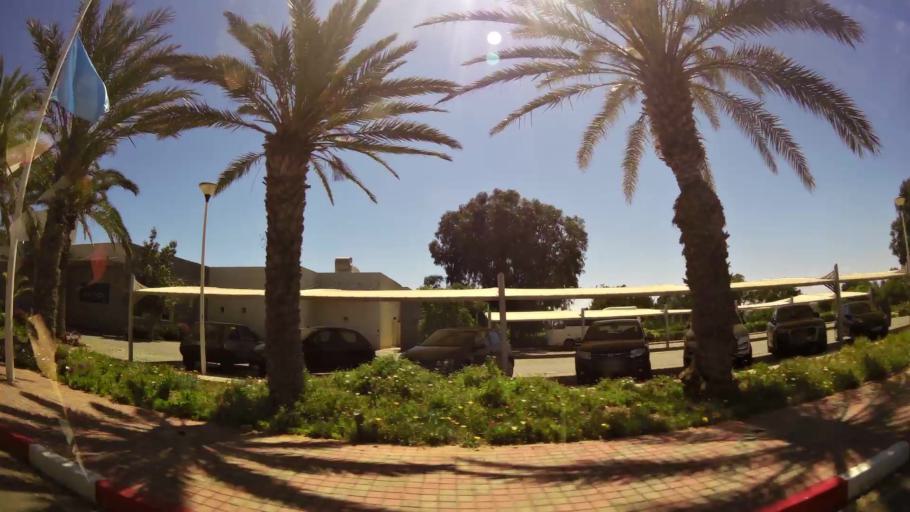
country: MA
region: Oriental
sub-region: Berkane-Taourirt
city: Madagh
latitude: 35.1104
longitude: -2.3103
